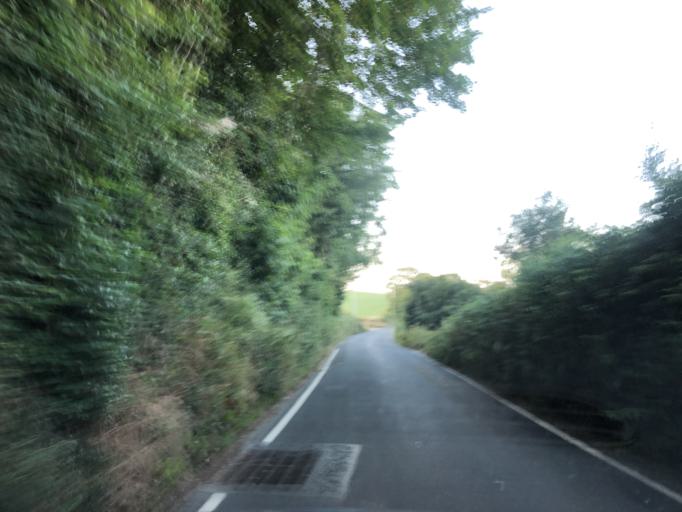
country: GB
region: England
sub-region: Isle of Wight
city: Niton
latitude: 50.5927
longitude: -1.2825
